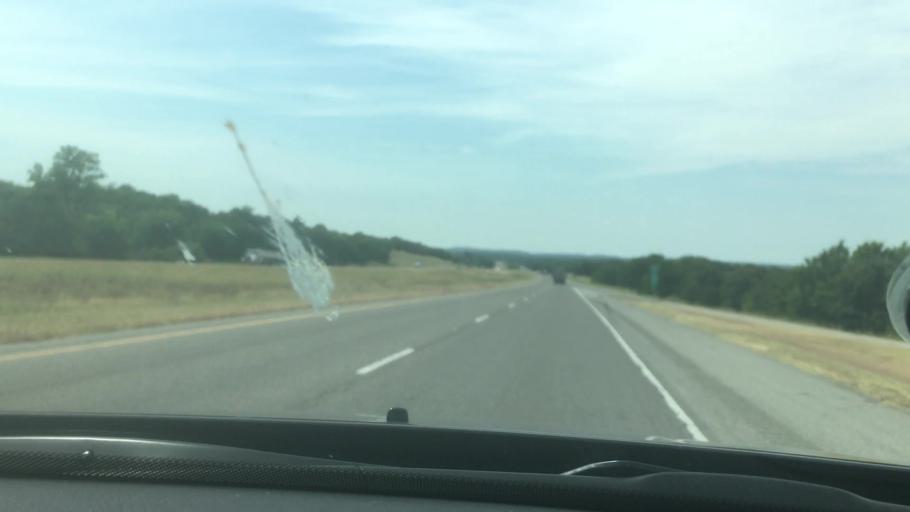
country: US
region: Oklahoma
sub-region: Murray County
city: Davis
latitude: 34.5461
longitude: -97.1906
